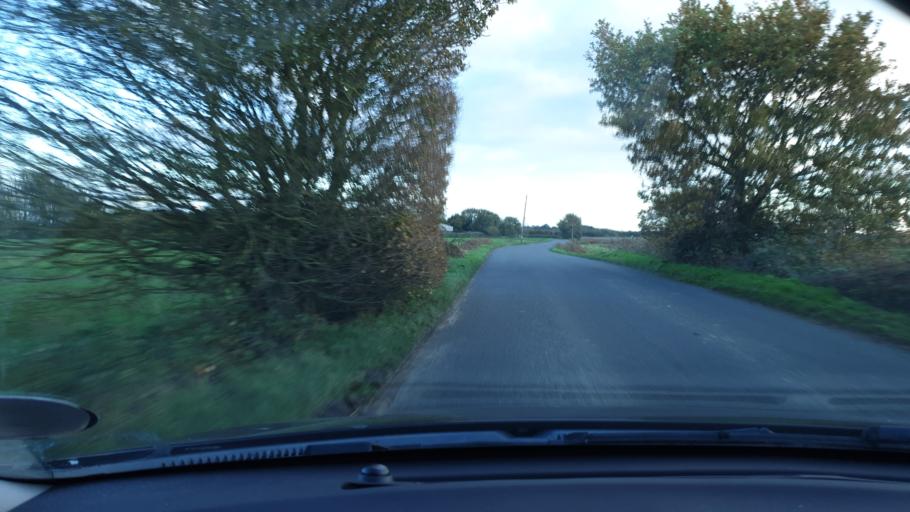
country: GB
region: England
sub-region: Essex
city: Little Clacton
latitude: 51.8922
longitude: 1.1487
